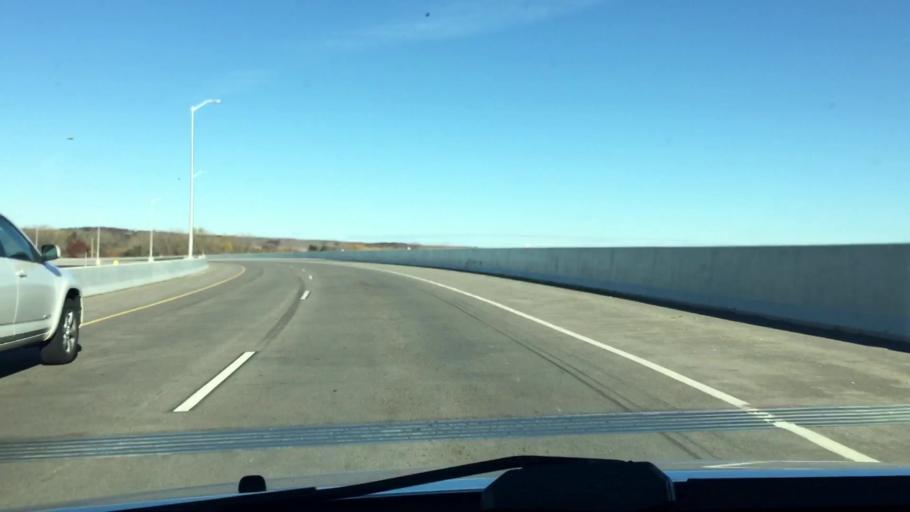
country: US
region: Wisconsin
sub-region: Brown County
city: Howard
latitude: 44.5383
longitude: -88.0787
